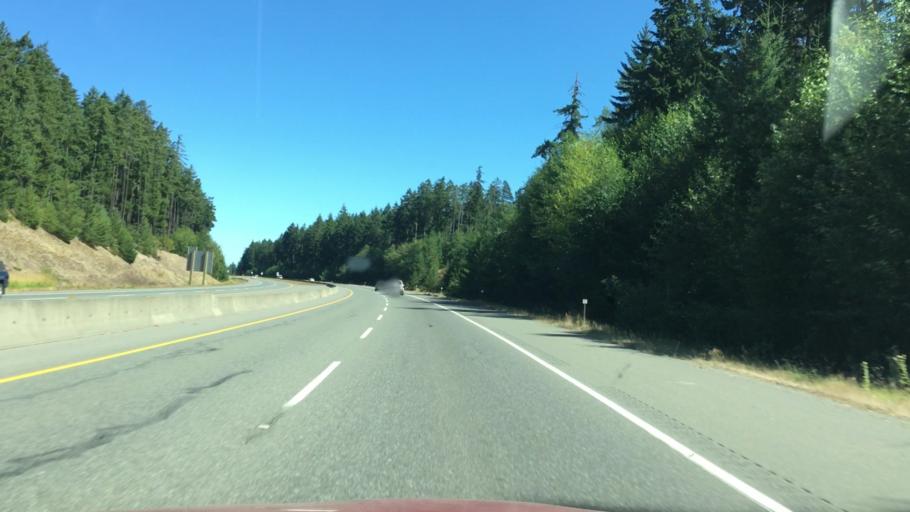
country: CA
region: British Columbia
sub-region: Regional District of Nanaimo
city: Parksville
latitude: 49.3198
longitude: -124.4053
